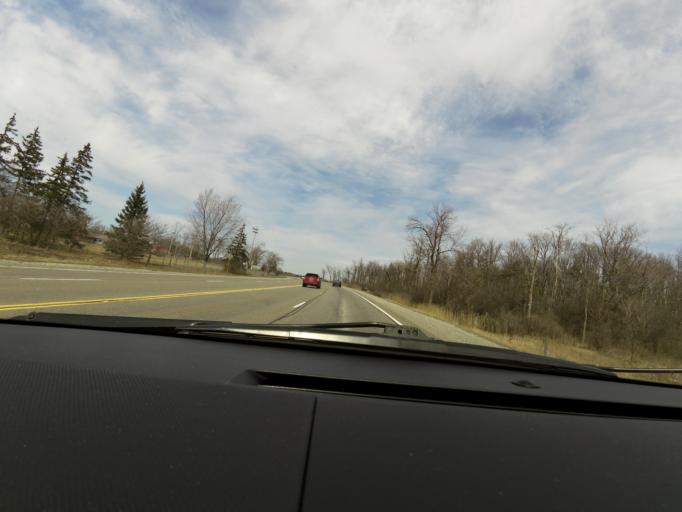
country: CA
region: Ontario
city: Ancaster
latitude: 43.1581
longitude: -79.9105
